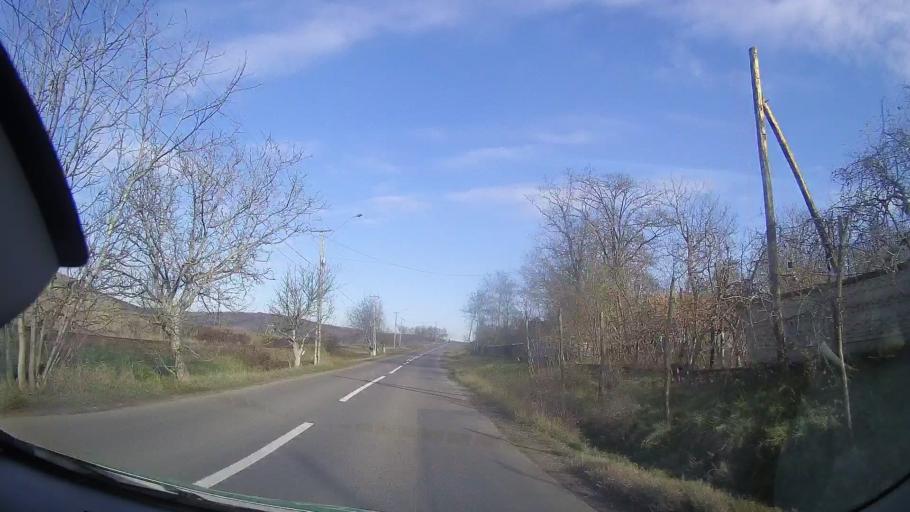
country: RO
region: Mures
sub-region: Comuna Valea Larga
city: Valea Larga
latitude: 46.5853
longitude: 24.0950
